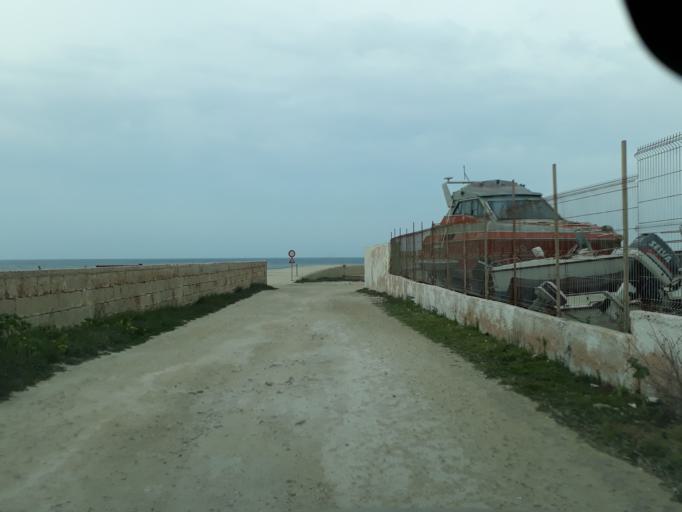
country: IT
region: Apulia
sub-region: Provincia di Brindisi
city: Ostuni
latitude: 40.7913
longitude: 17.5853
